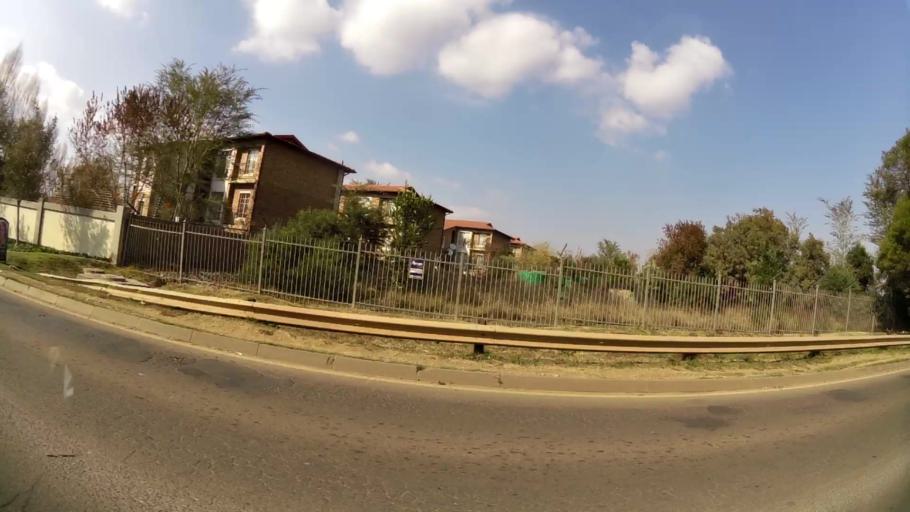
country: ZA
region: Gauteng
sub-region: City of Tshwane Metropolitan Municipality
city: Pretoria
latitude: -25.7816
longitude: 28.3625
